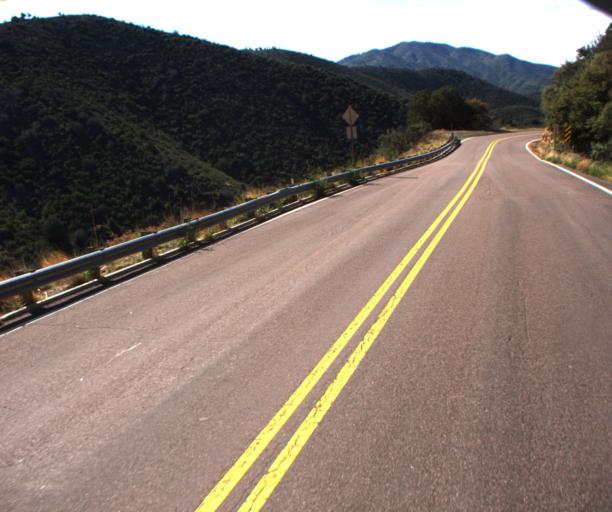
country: US
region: Arizona
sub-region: Yavapai County
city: Prescott
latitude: 34.4672
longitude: -112.5151
